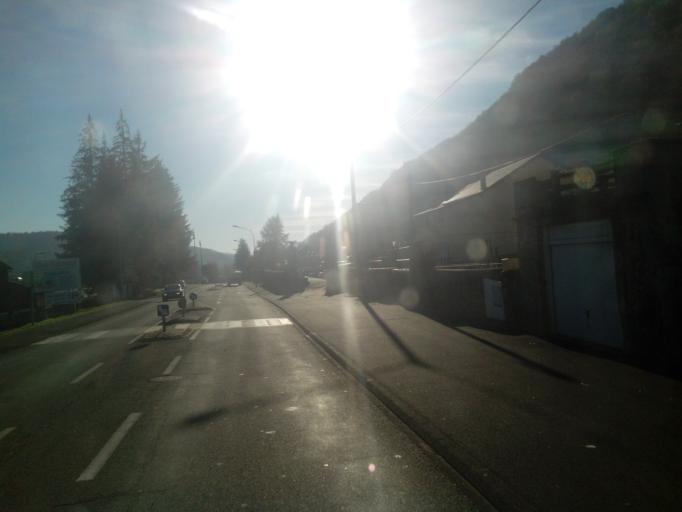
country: FR
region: Limousin
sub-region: Departement de la Correze
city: Bort-les-Orgues
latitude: 45.3994
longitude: 2.4930
